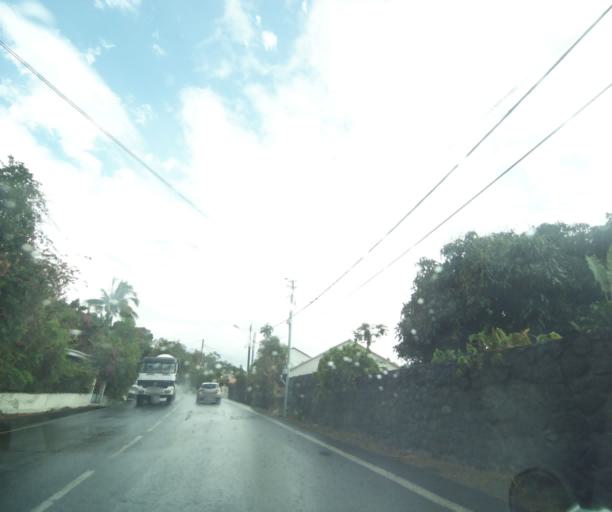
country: RE
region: Reunion
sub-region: Reunion
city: La Possession
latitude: -20.9837
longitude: 55.3340
